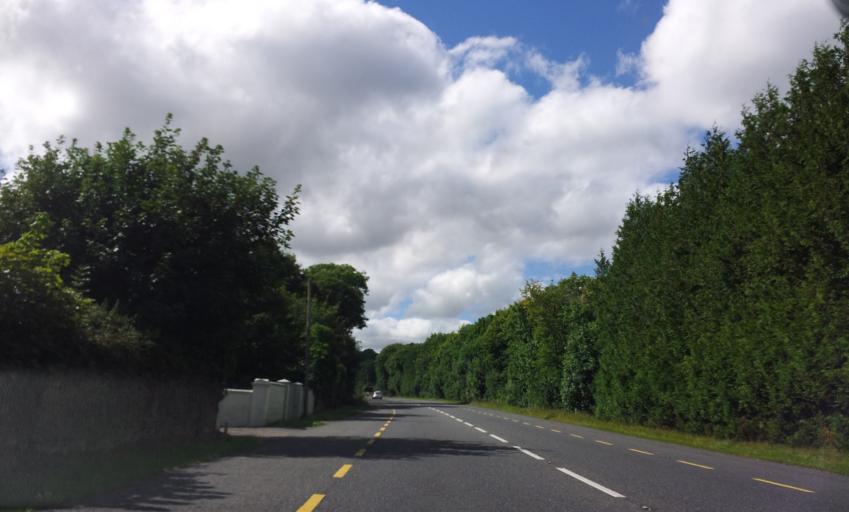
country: IE
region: Munster
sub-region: County Cork
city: Killumney
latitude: 51.8818
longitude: -8.6644
